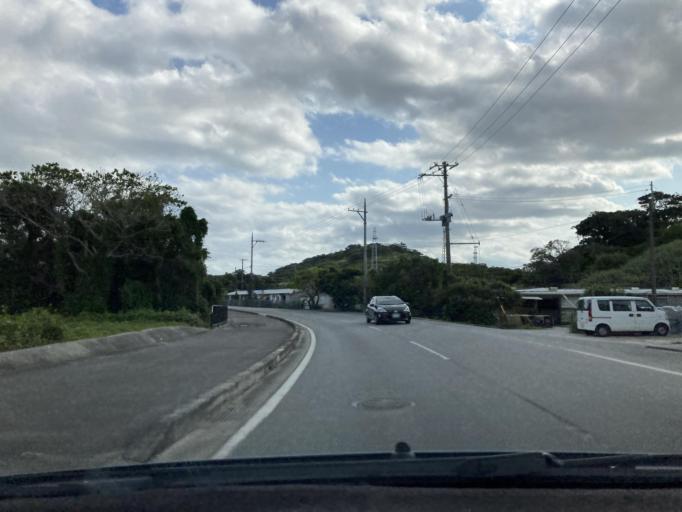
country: JP
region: Okinawa
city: Tomigusuku
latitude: 26.1777
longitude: 127.7609
